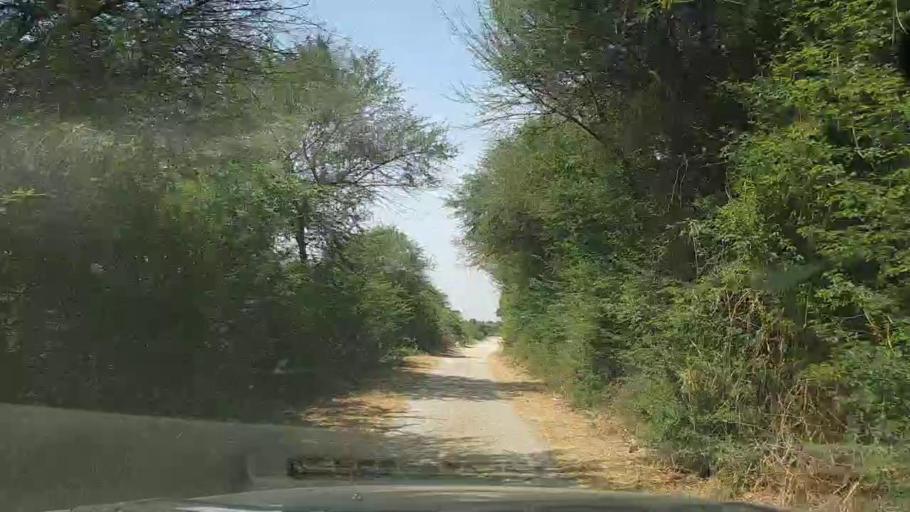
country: PK
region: Sindh
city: Mirpur Batoro
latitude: 24.6524
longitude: 68.1693
